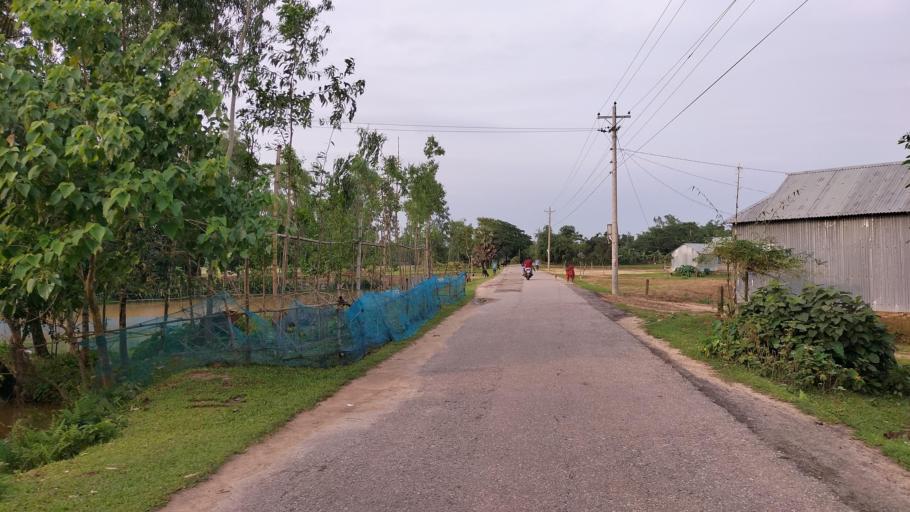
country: BD
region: Dhaka
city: Netrakona
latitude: 25.1351
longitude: 90.9162
